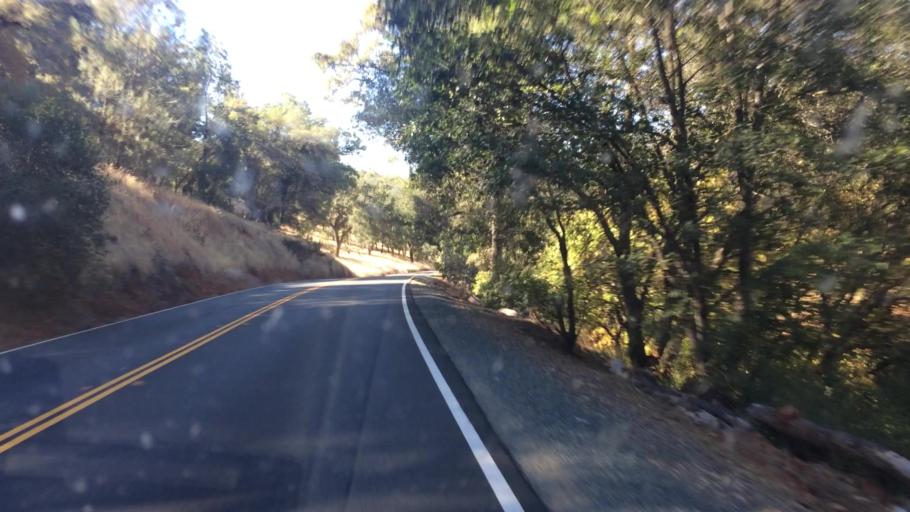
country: US
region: California
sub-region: El Dorado County
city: Deer Park
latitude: 38.6197
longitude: -120.8514
